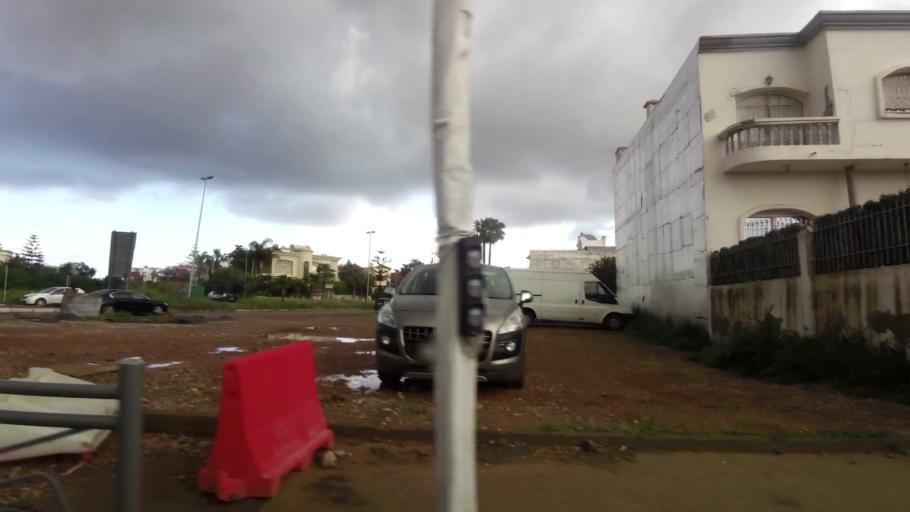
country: MA
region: Grand Casablanca
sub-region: Casablanca
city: Casablanca
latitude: 33.5450
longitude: -7.6618
